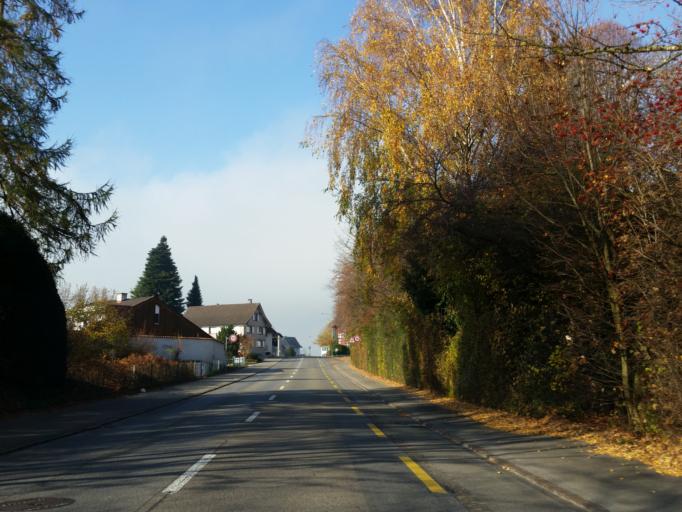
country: CH
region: Thurgau
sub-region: Arbon District
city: Arbon
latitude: 47.5263
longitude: 9.4074
